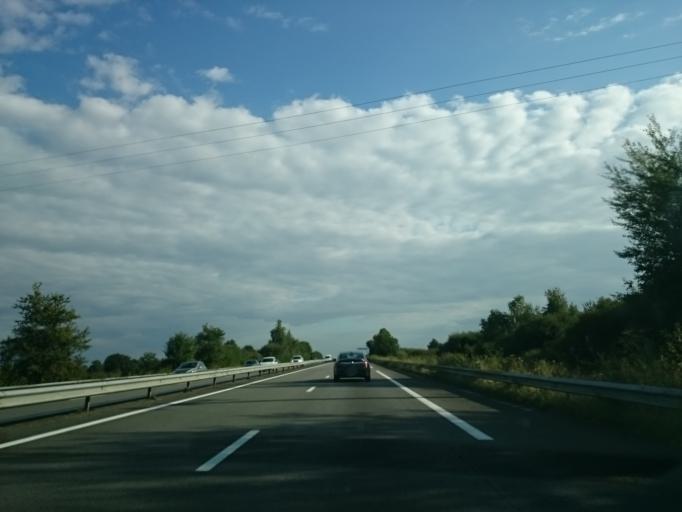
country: FR
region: Pays de la Loire
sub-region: Departement de la Loire-Atlantique
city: Treillieres
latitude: 47.3439
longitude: -1.6550
